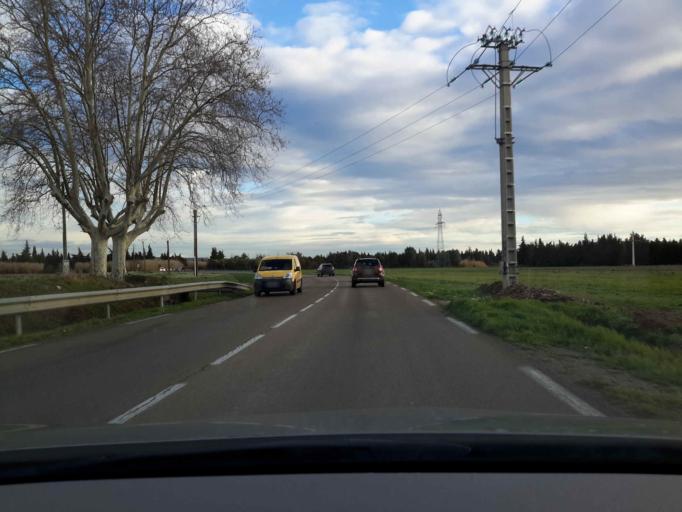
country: FR
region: Languedoc-Roussillon
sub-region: Departement du Gard
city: Caissargues
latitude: 43.7983
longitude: 4.3532
